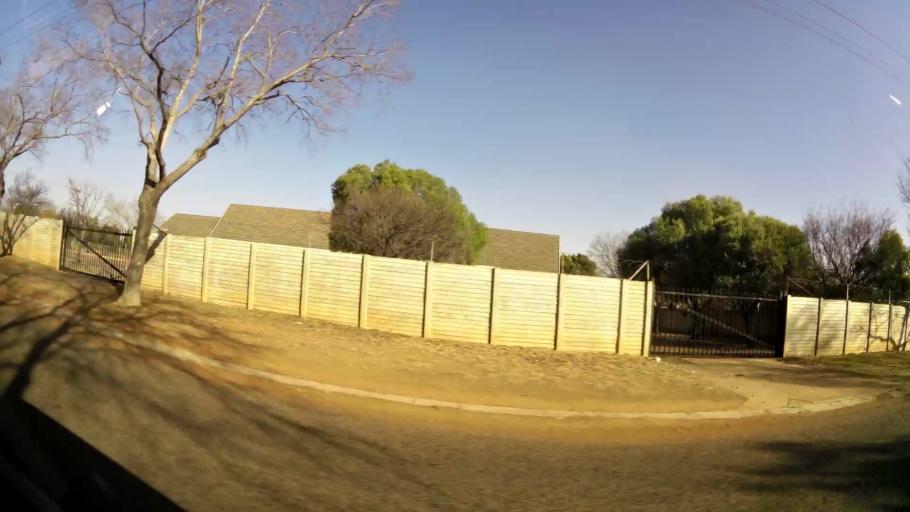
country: ZA
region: Gauteng
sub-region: City of Tshwane Metropolitan Municipality
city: Pretoria
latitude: -25.7081
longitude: 28.2449
